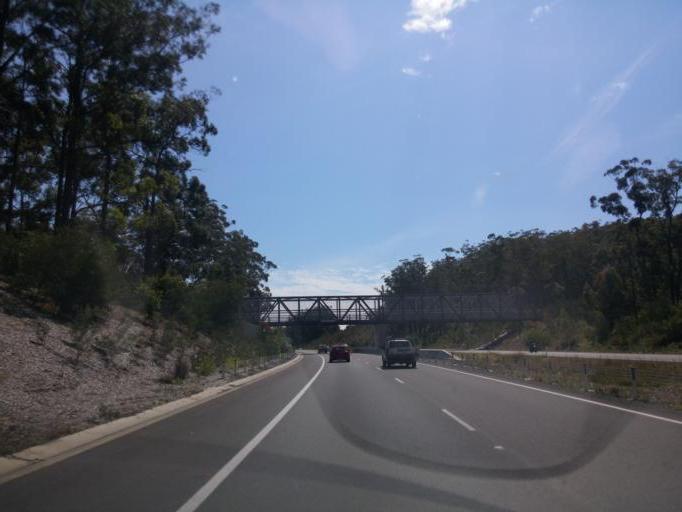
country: AU
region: New South Wales
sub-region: Great Lakes
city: Bulahdelah
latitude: -32.4152
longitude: 152.2163
